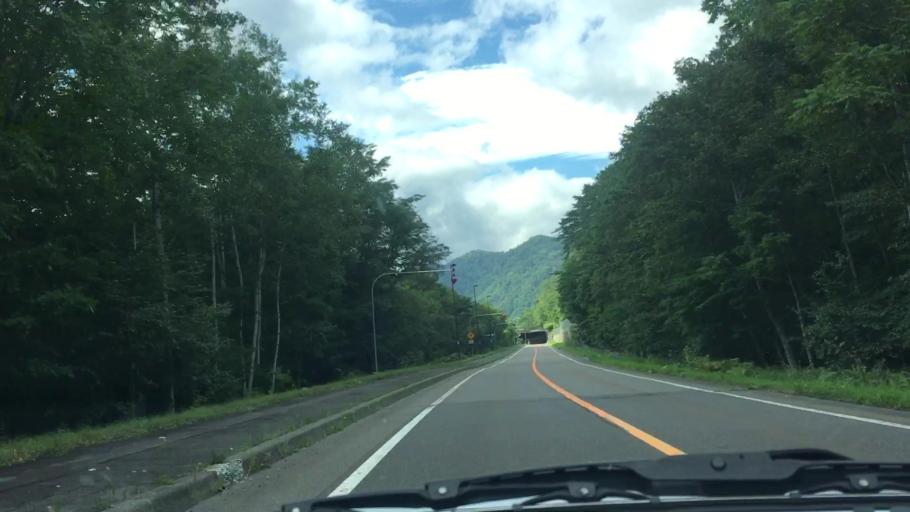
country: JP
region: Hokkaido
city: Otofuke
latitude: 43.3516
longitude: 143.2644
